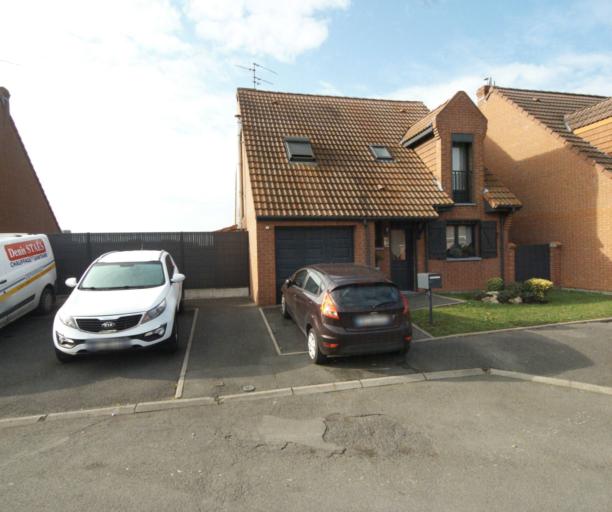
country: FR
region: Nord-Pas-de-Calais
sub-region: Departement du Nord
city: Wattignies
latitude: 50.5991
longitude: 3.0484
